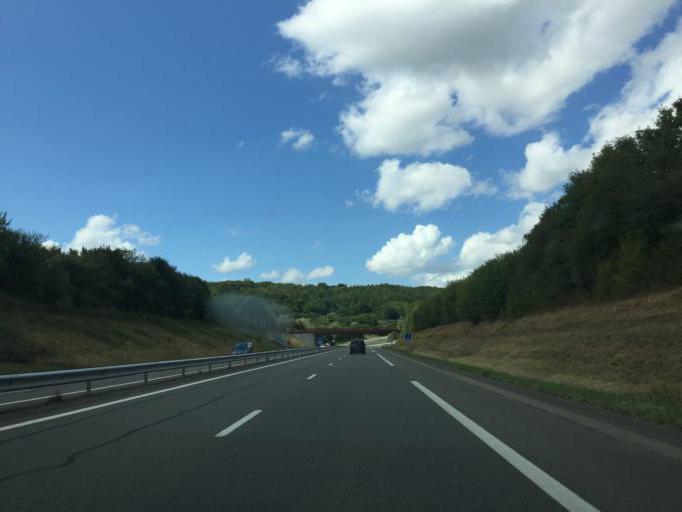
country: FR
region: Bourgogne
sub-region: Departement de Saone-et-Loire
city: Sance
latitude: 46.3468
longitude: 4.8317
